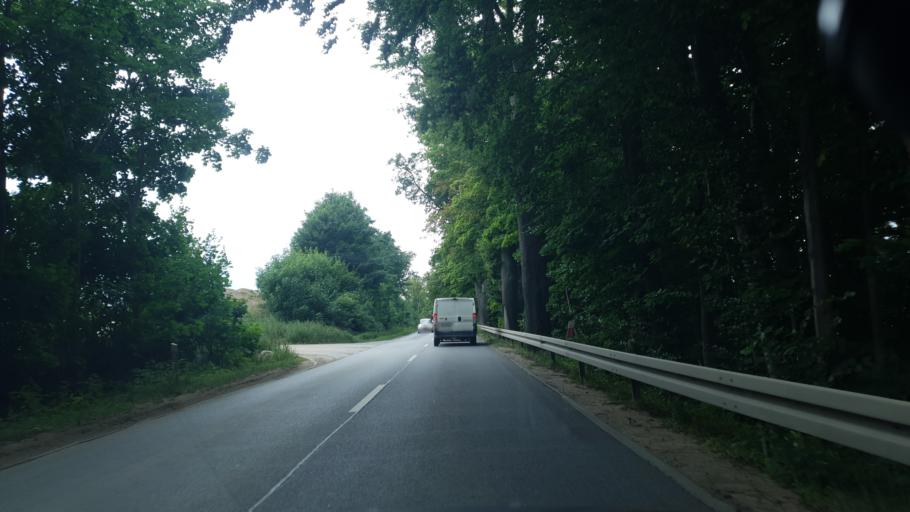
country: PL
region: Pomeranian Voivodeship
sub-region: Powiat kartuski
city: Przodkowo
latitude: 54.3847
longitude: 18.3276
